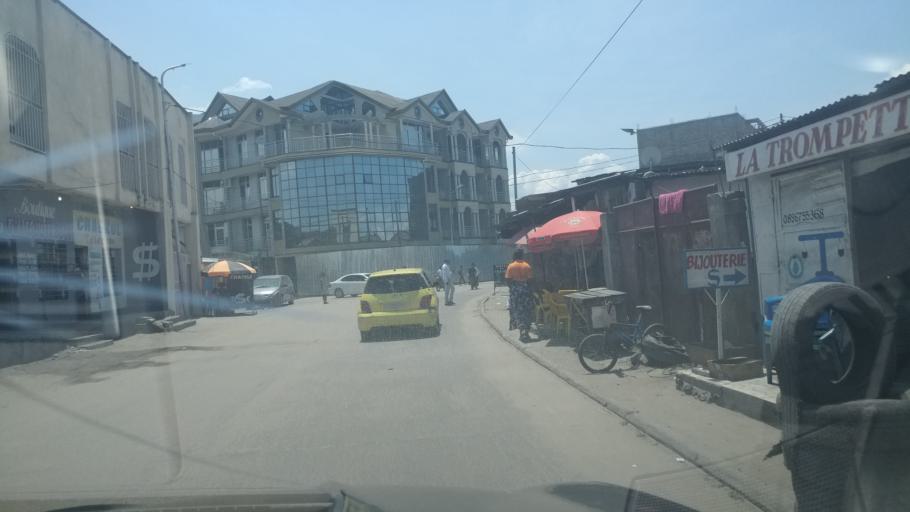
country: CD
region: Kinshasa
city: Kinshasa
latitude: -4.3364
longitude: 15.2646
